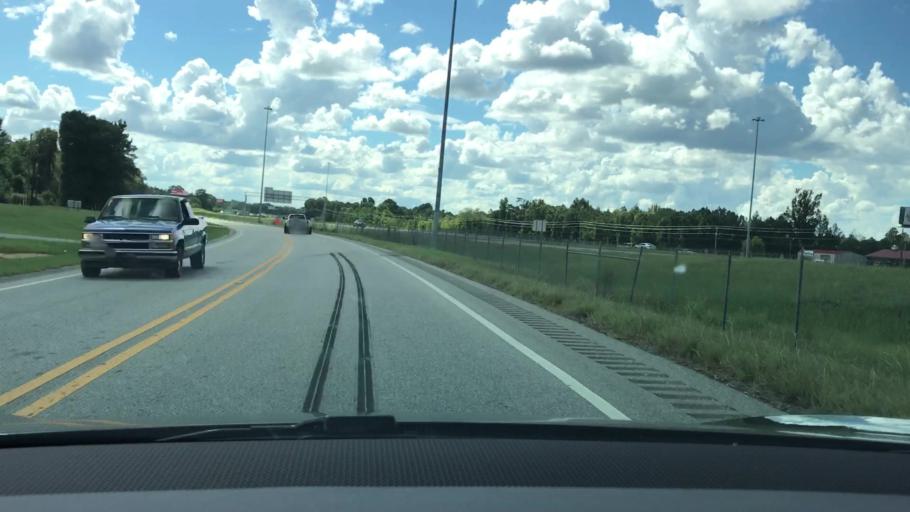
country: US
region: Alabama
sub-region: Montgomery County
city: Pike Road
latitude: 32.3664
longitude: -86.0869
